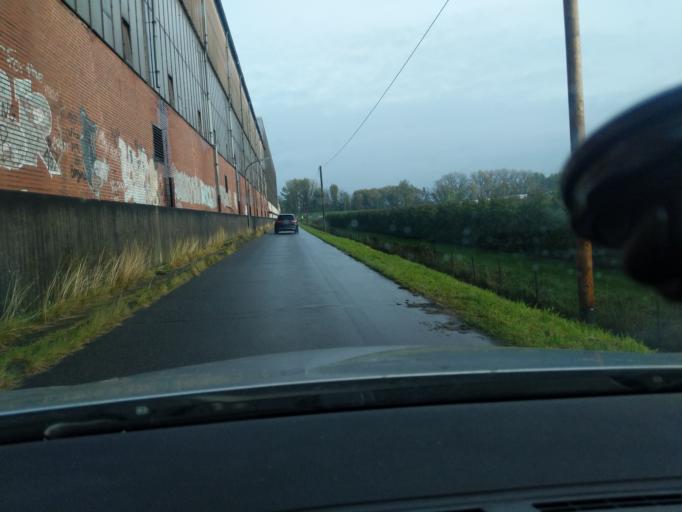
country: DE
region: Lower Saxony
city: Neu Wulmstorf
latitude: 53.5310
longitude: 9.7918
